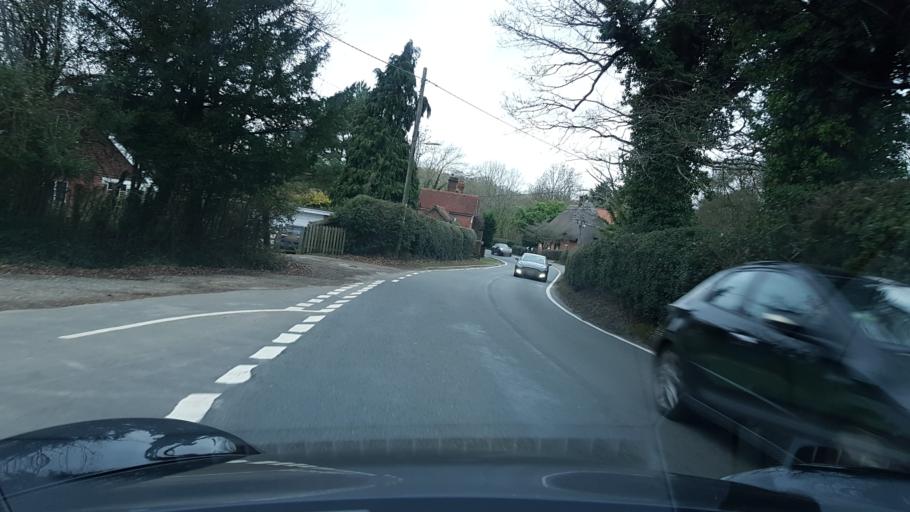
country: GB
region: England
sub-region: Hampshire
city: Cadnam
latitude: 50.9247
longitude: -1.6105
